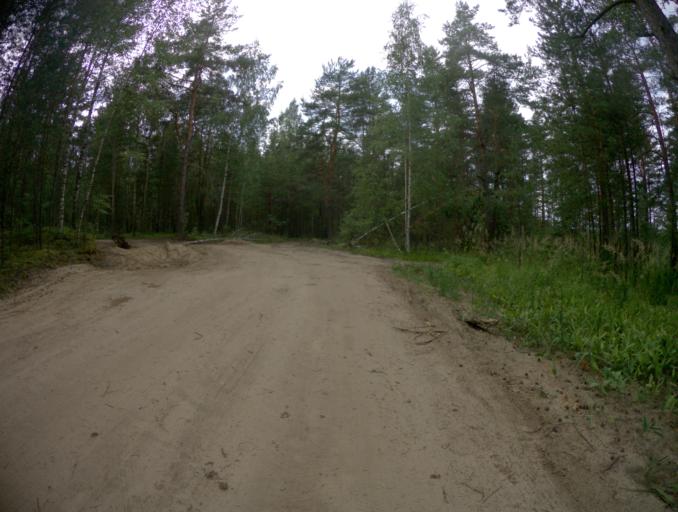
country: RU
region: Nizjnij Novgorod
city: Frolishchi
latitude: 56.3510
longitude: 42.7513
